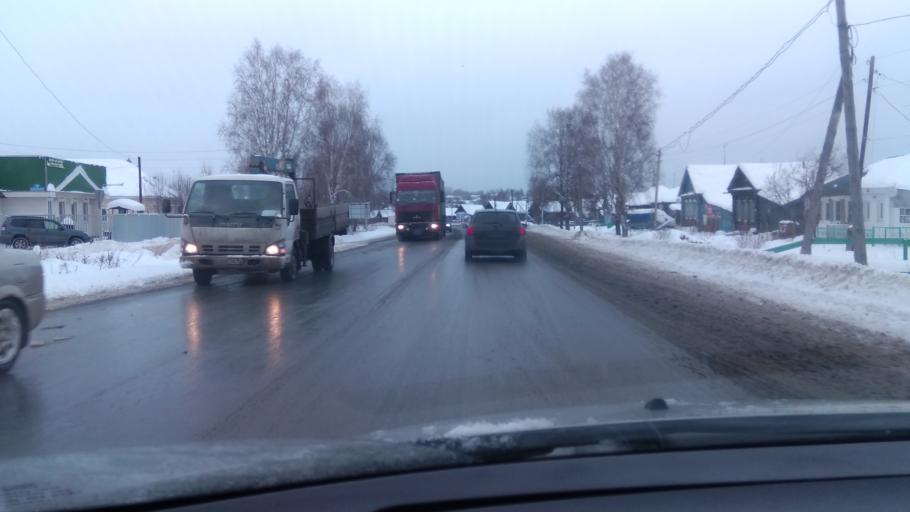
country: RU
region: Sverdlovsk
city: Nikolo-Pavlovskoye
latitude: 57.7819
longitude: 60.0601
